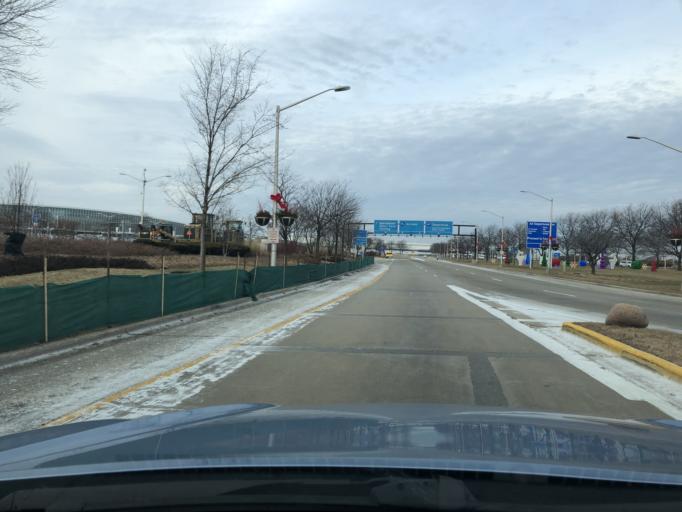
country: US
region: Illinois
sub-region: Cook County
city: Rosemont
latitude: 41.9759
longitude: -87.8865
